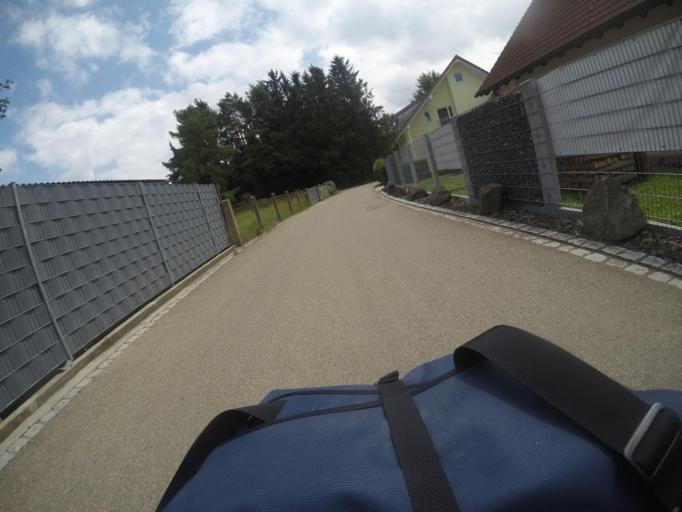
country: DE
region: Bavaria
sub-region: Swabia
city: Heimertingen
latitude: 48.0360
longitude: 10.1601
